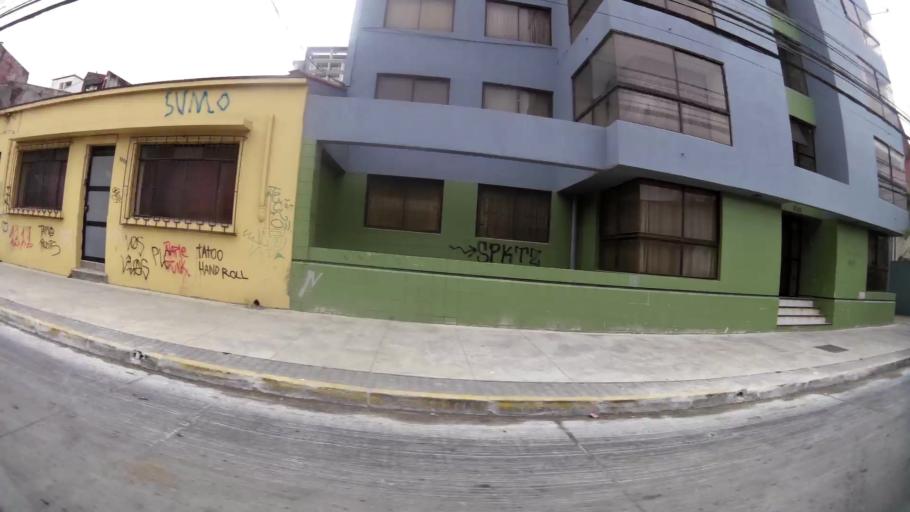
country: CL
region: Biobio
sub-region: Provincia de Concepcion
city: Concepcion
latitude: -36.8197
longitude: -73.0401
